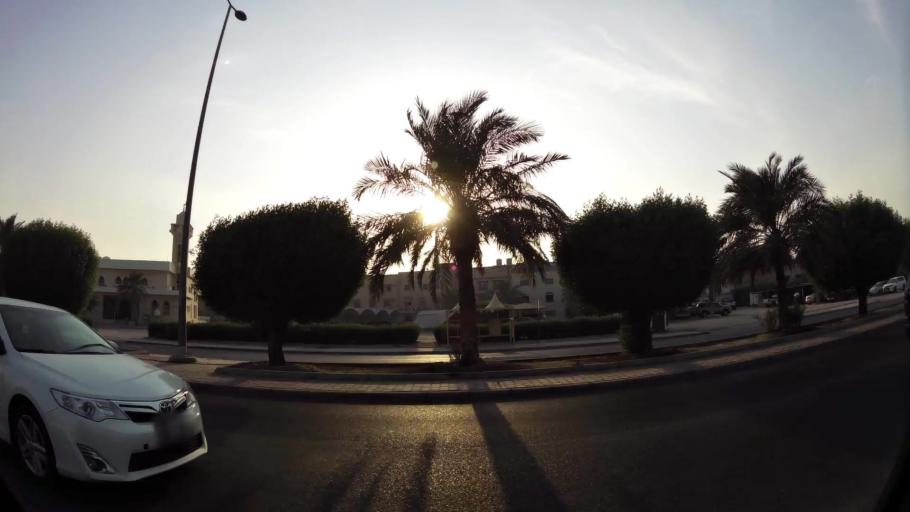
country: KW
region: Mubarak al Kabir
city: Sabah as Salim
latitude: 29.2465
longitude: 48.0694
